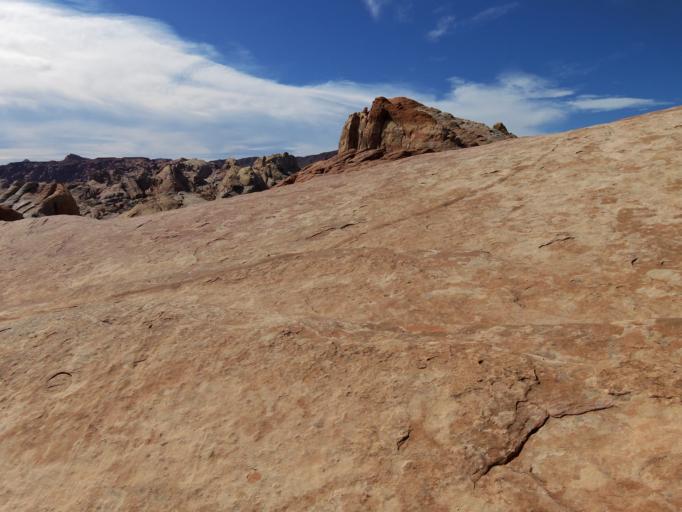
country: US
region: Nevada
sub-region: Clark County
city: Moapa Valley
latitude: 36.4874
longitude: -114.5293
